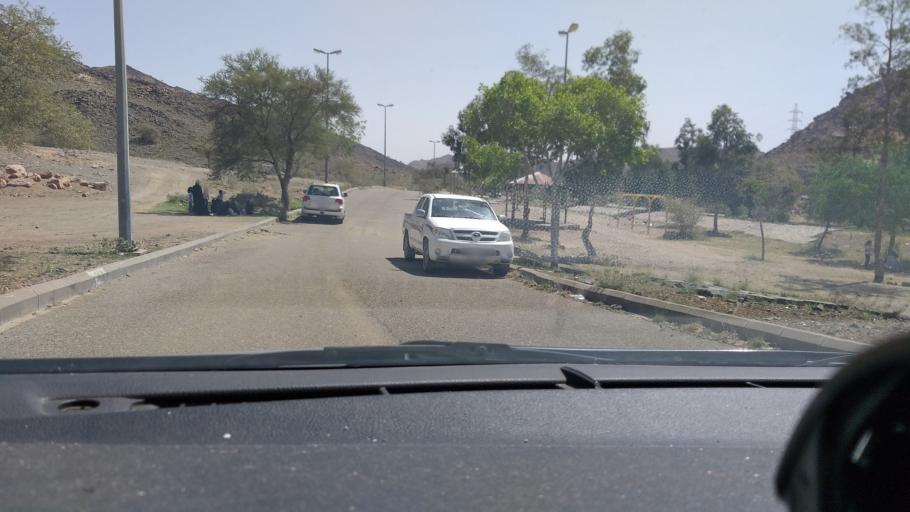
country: SA
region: Makkah
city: Ash Shafa
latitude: 21.1603
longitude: 40.3703
